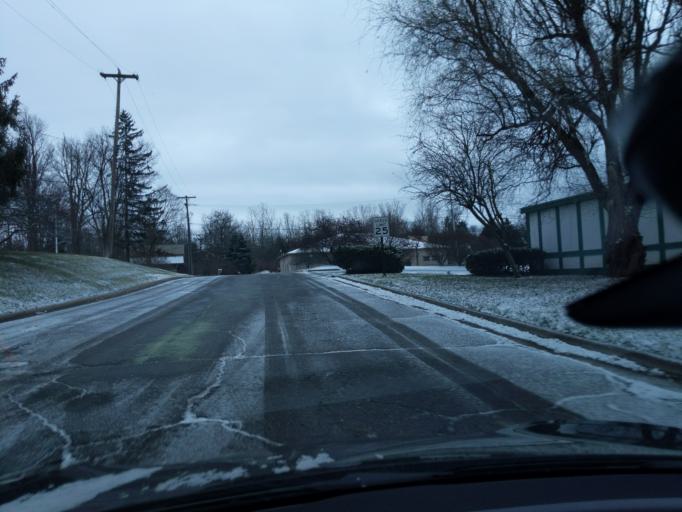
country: US
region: Michigan
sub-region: Ingham County
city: Okemos
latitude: 42.7179
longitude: -84.4284
